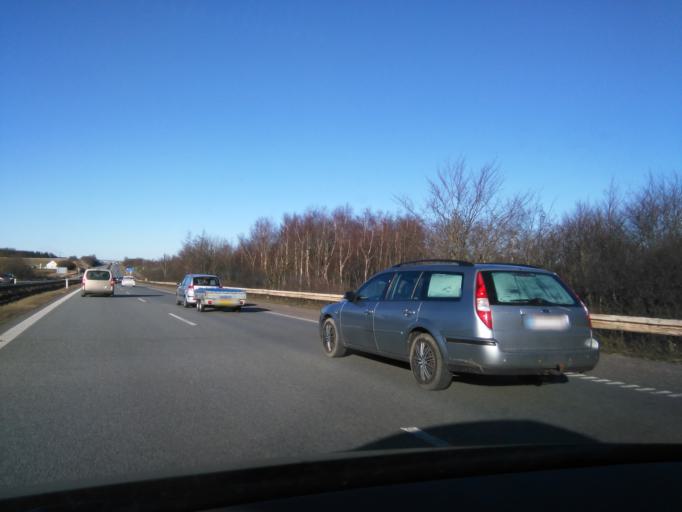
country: DK
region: Central Jutland
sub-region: Randers Kommune
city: Randers
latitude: 56.4778
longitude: 9.9816
